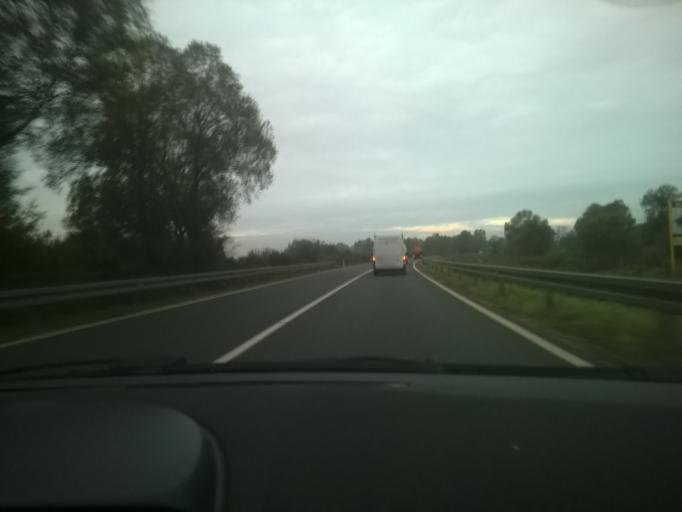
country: HR
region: Zagrebacka
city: Jakovlje
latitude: 45.9644
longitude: 15.8441
